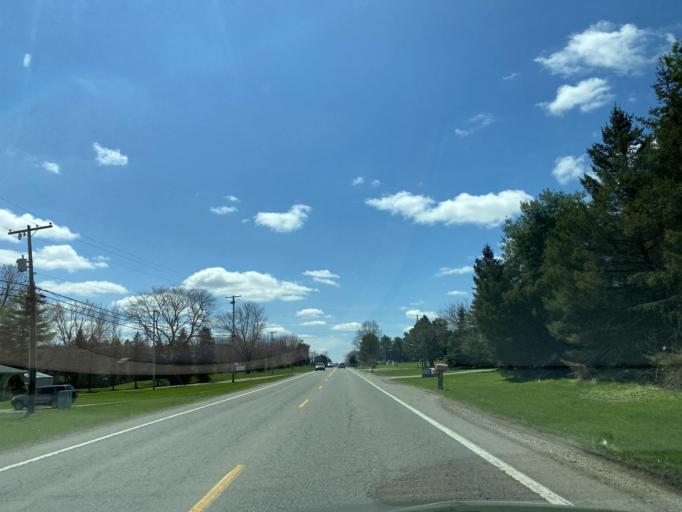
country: US
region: Ohio
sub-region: Wayne County
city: Shreve
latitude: 40.7395
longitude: -81.9883
